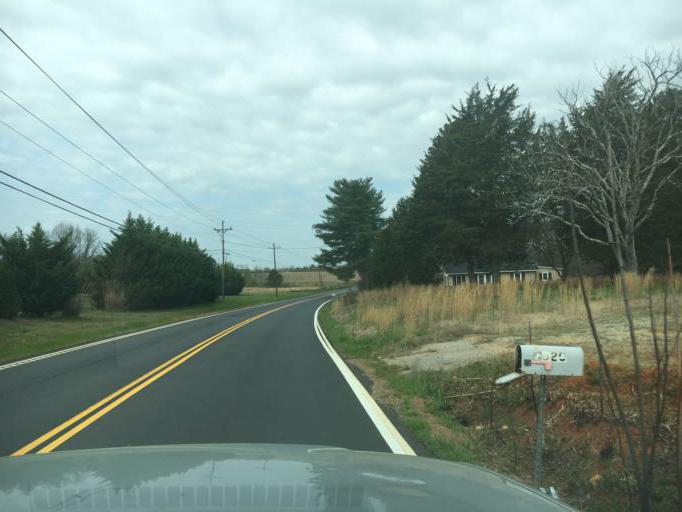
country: US
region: South Carolina
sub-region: Spartanburg County
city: Inman Mills
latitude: 35.0606
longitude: -82.1634
